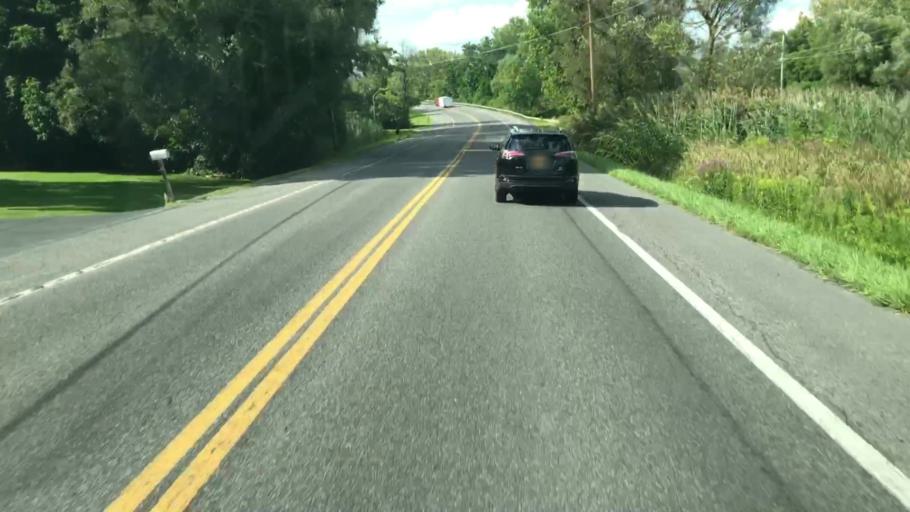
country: US
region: New York
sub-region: Onondaga County
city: Liverpool
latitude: 43.1677
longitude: -76.1959
